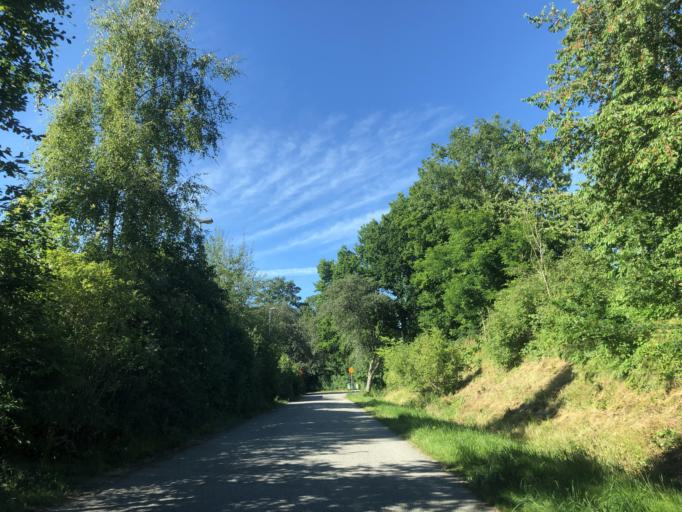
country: SE
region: Skane
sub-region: Eslovs Kommun
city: Stehag
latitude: 55.9637
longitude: 13.3264
